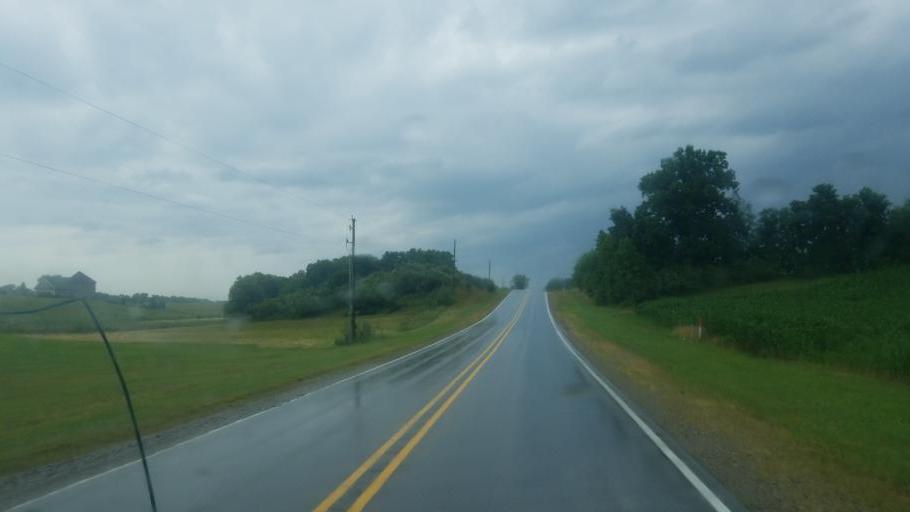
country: US
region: Indiana
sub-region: Steuben County
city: Hamilton
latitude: 41.5007
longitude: -84.8728
